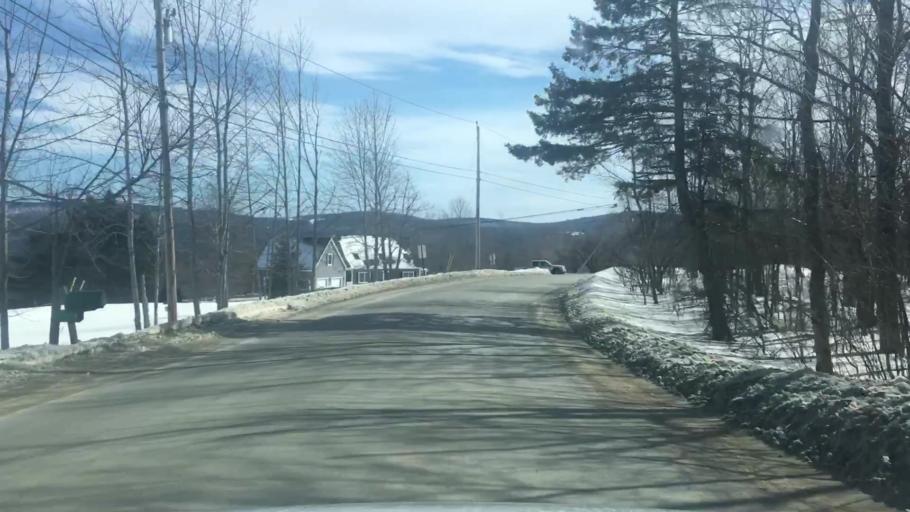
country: US
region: Maine
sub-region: Penobscot County
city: Holden
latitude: 44.7649
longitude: -68.6433
